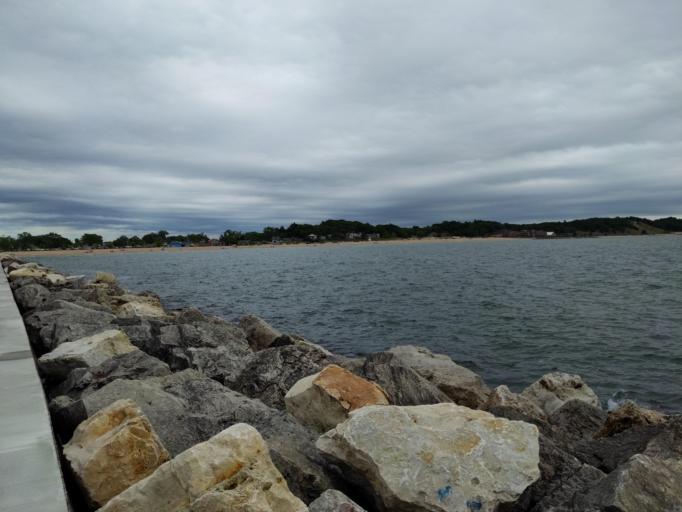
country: US
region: Michigan
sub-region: Muskegon County
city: Roosevelt Park
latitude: 43.2228
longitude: -86.3418
